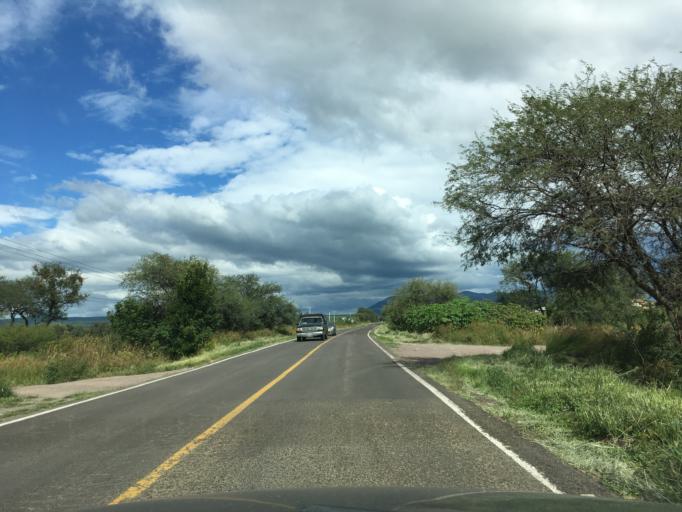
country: MX
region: Michoacan
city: Santa Ana Maya
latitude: 20.0449
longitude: -101.0707
